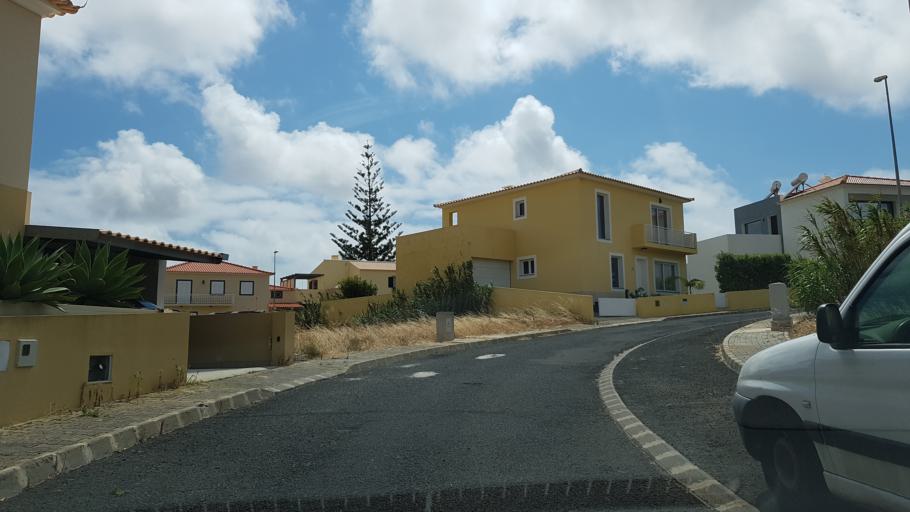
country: PT
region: Madeira
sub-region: Porto Santo
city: Vila de Porto Santo
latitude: 33.0582
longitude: -16.3437
